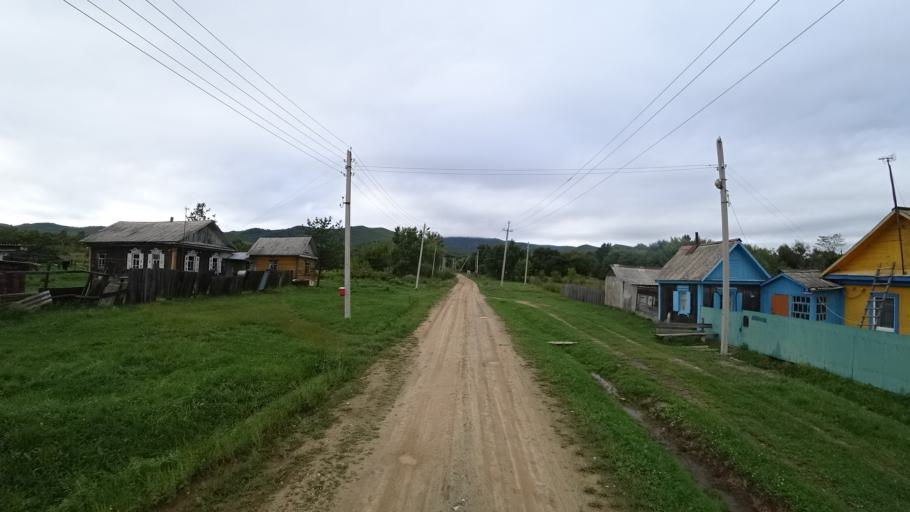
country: RU
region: Primorskiy
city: Rettikhovka
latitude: 44.1402
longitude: 132.6417
